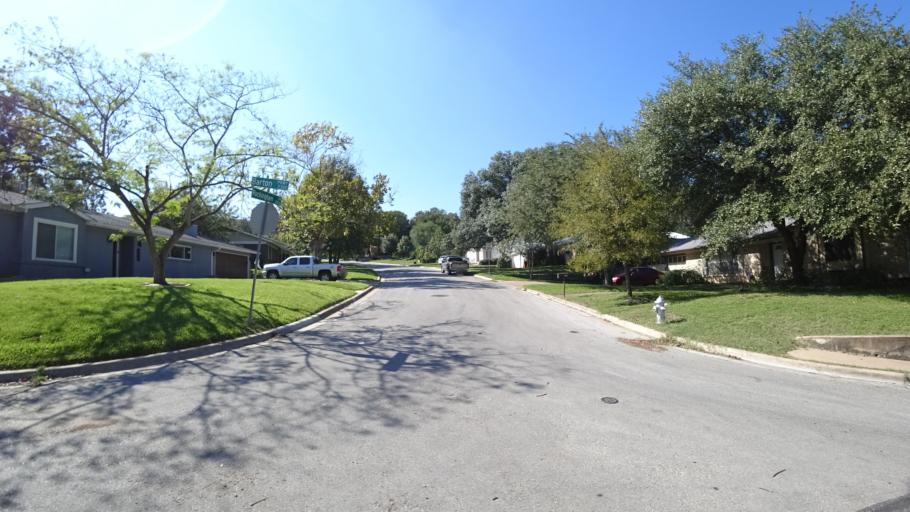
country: US
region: Texas
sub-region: Travis County
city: Rollingwood
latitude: 30.2515
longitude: -97.7829
